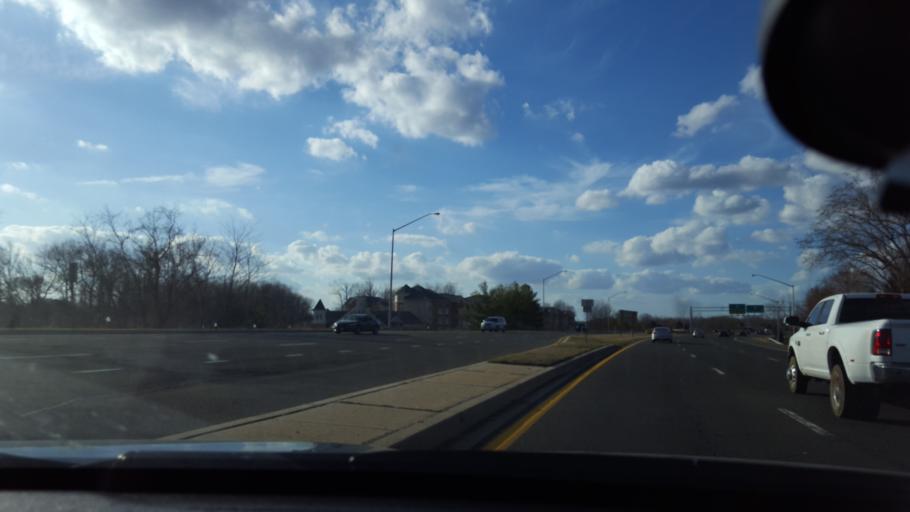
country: US
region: Maryland
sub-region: Prince George's County
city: Bowie
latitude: 38.9482
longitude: -76.7386
